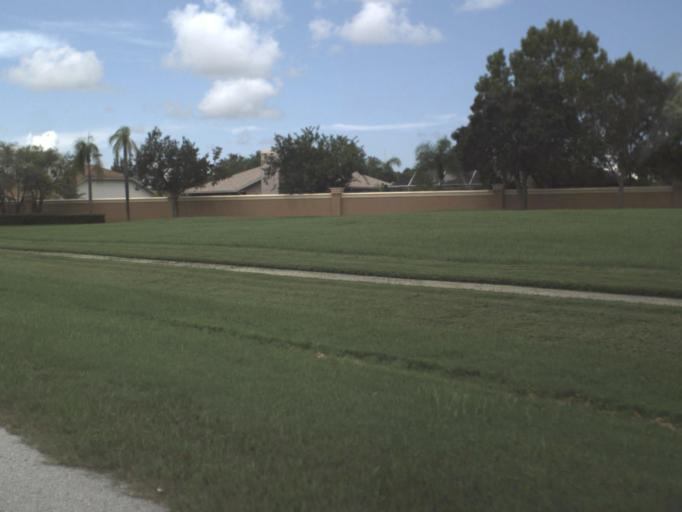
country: US
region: Florida
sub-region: Pinellas County
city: Saint George
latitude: 28.0740
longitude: -82.7042
